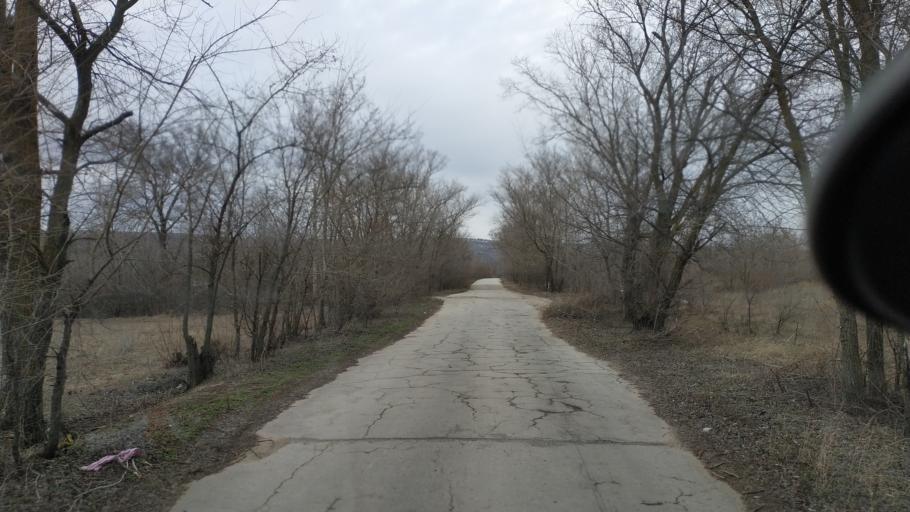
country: MD
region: Telenesti
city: Cocieri
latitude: 47.3284
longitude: 29.0920
